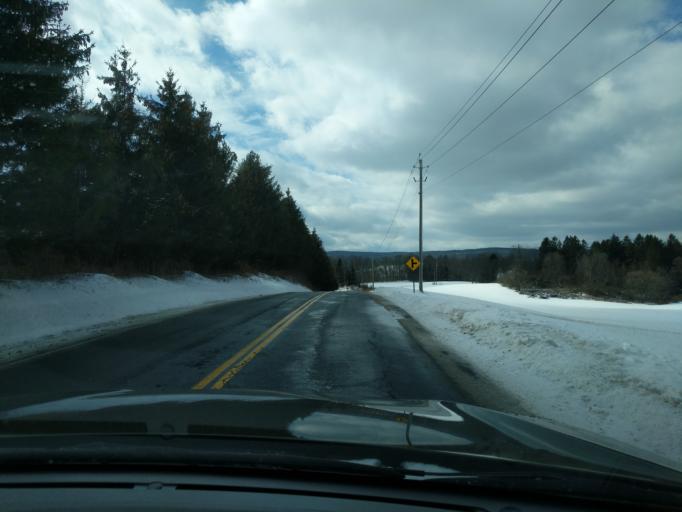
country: US
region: New York
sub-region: Tompkins County
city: East Ithaca
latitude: 42.3852
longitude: -76.3837
